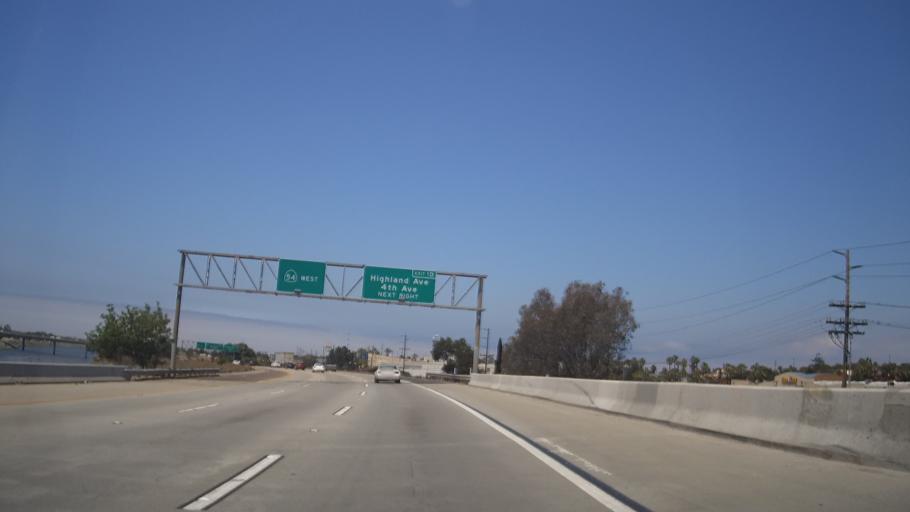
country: US
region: California
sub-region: San Diego County
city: Chula Vista
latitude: 32.6593
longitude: -117.0830
